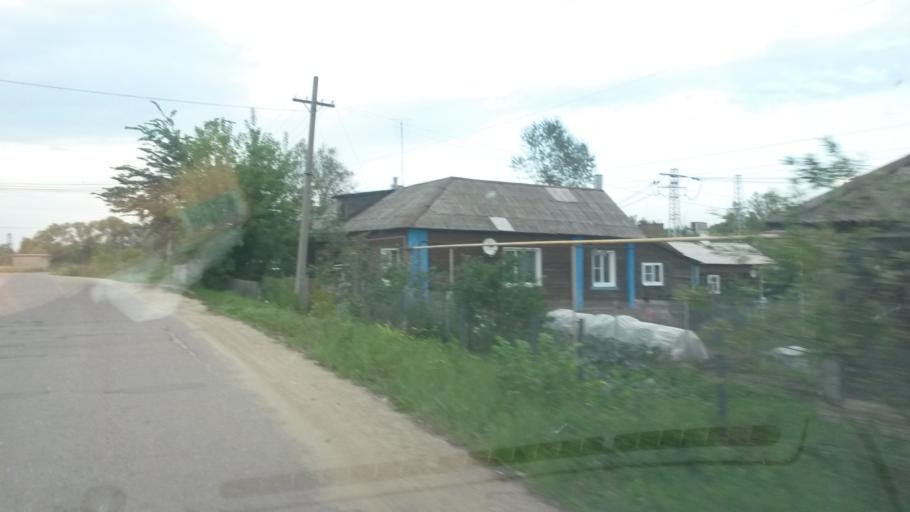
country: RU
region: Jaroslavl
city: Petrovsk
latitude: 56.9983
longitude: 39.2703
